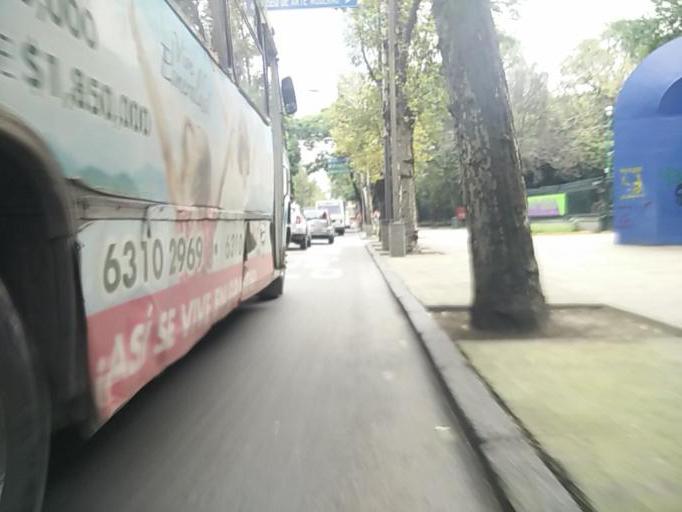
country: MX
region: Mexico City
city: Polanco
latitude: 19.4238
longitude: -99.1801
